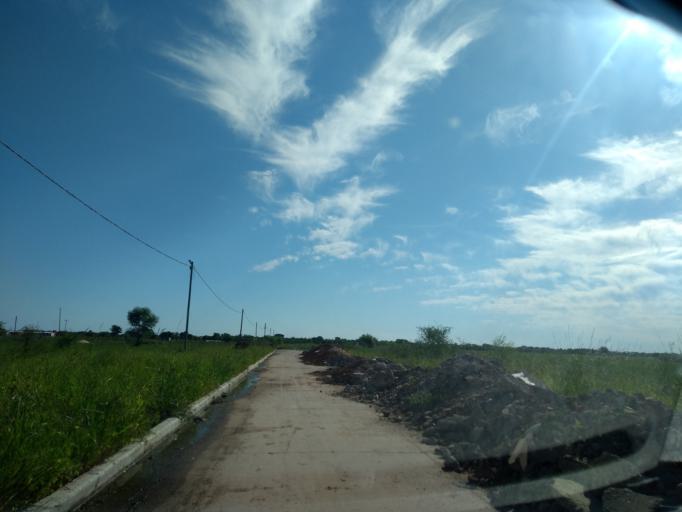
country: AR
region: Chaco
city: Resistencia
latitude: -27.4824
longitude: -59.0143
